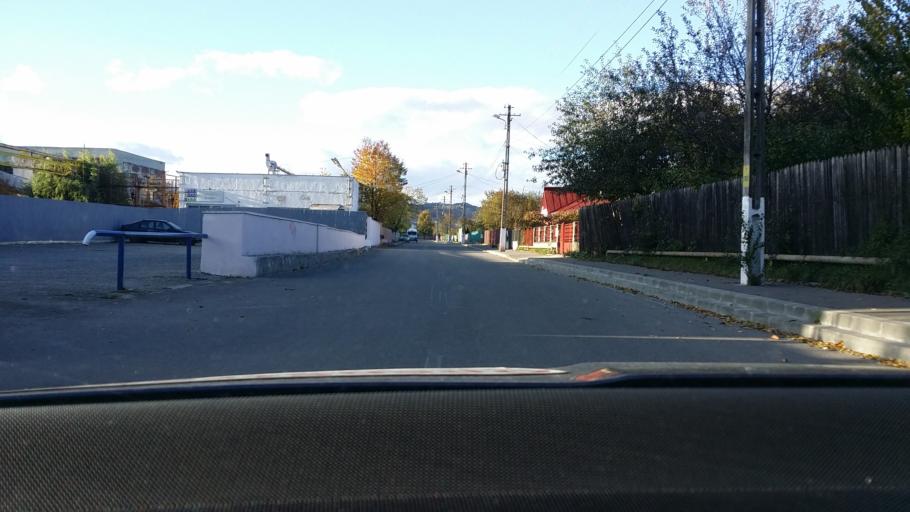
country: RO
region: Prahova
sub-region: Municipiul Campina
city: Campina
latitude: 45.1363
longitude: 25.7414
